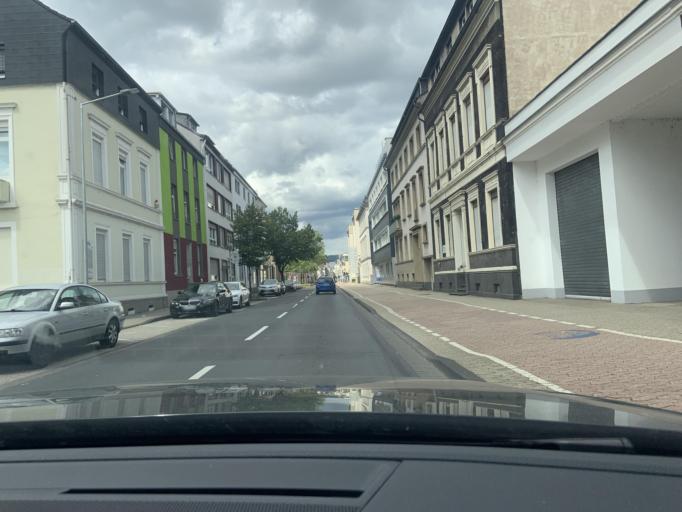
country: DE
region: Rheinland-Pfalz
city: Neuwied
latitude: 50.4269
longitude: 7.4657
